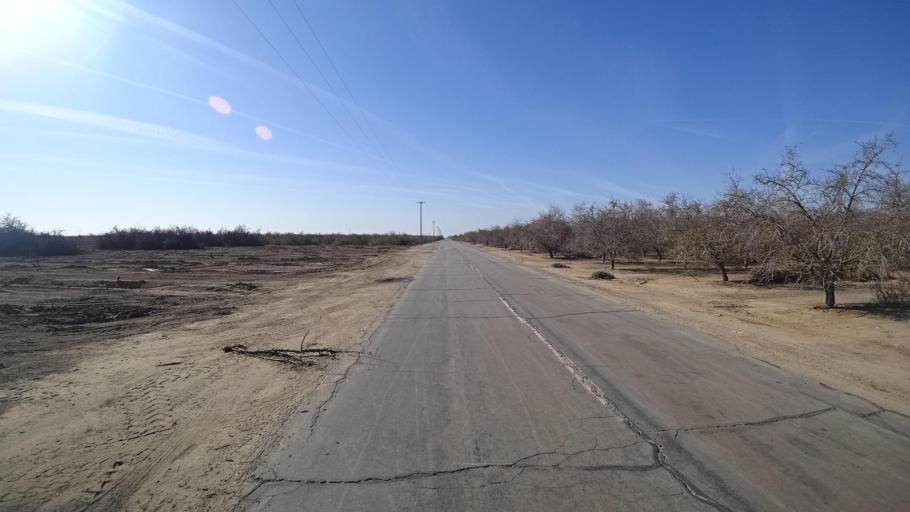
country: US
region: California
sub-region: Kern County
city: Wasco
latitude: 35.6669
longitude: -119.3446
